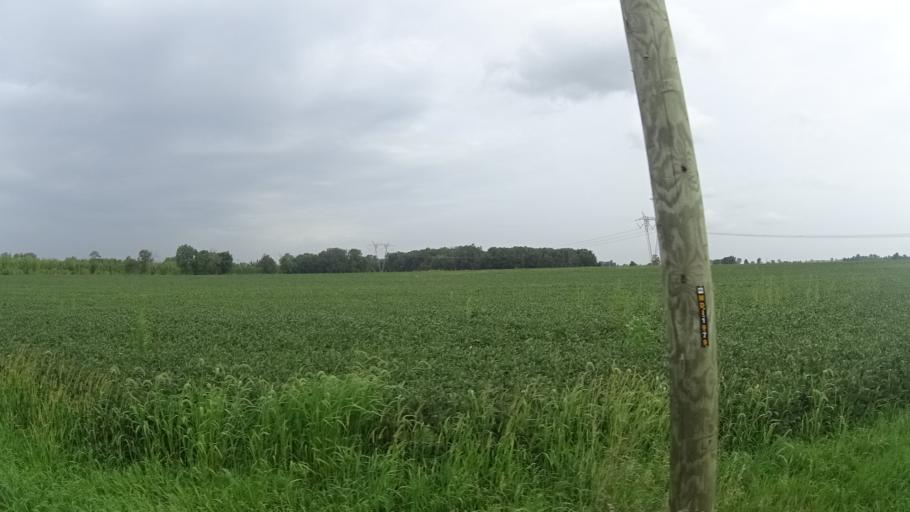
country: US
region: Indiana
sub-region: Madison County
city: Ingalls
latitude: 40.0024
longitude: -85.8266
